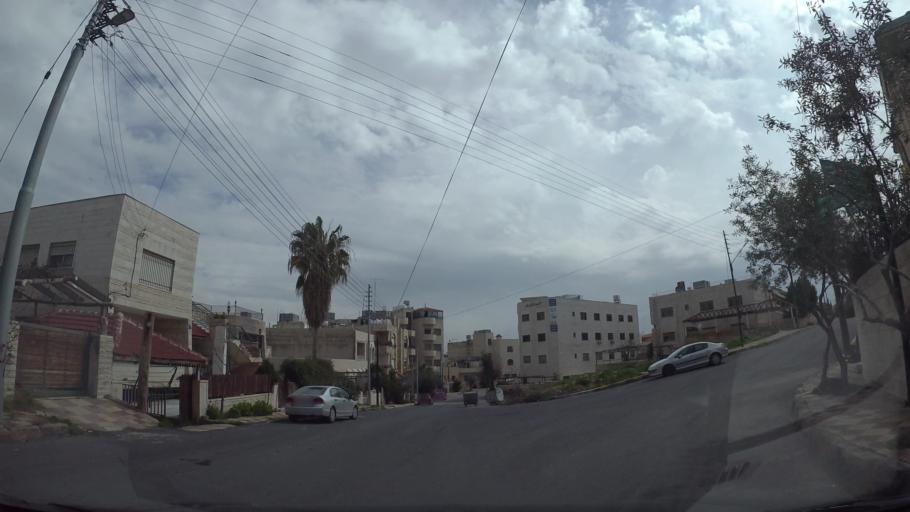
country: JO
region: Amman
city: Amman
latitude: 31.9990
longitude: 35.9369
